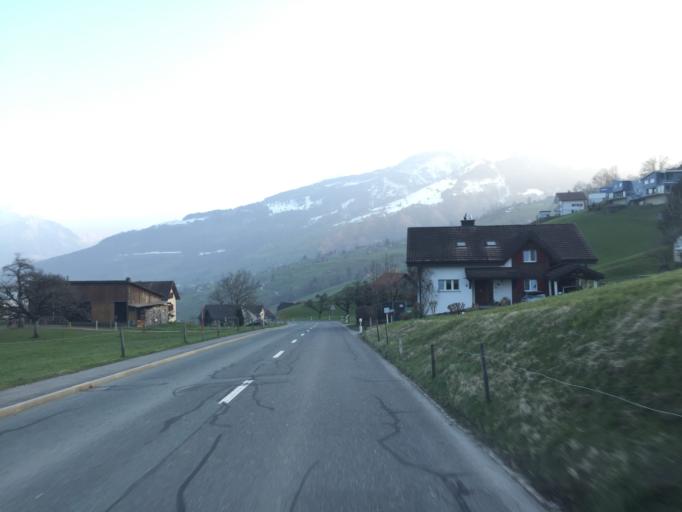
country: CH
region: Saint Gallen
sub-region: Wahlkreis Werdenberg
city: Gams
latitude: 47.2010
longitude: 9.4318
